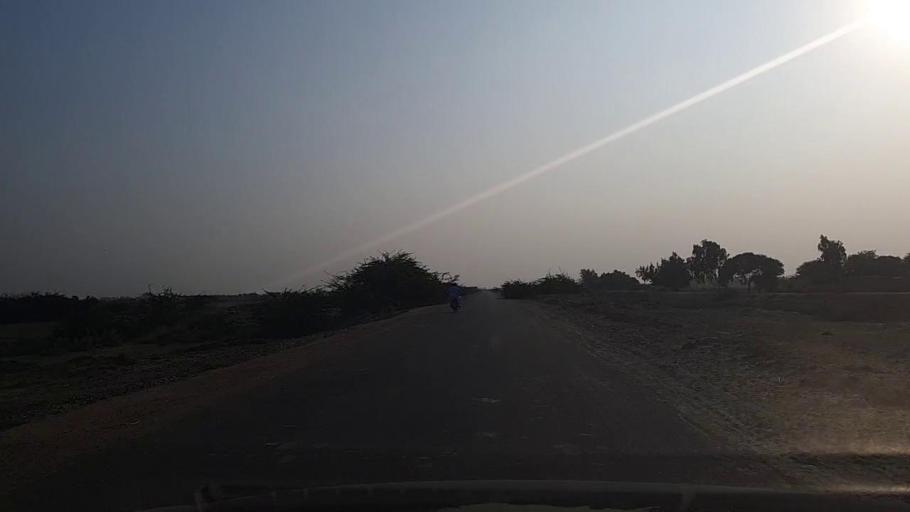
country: PK
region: Sindh
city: Mirpur Sakro
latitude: 24.4910
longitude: 67.8095
